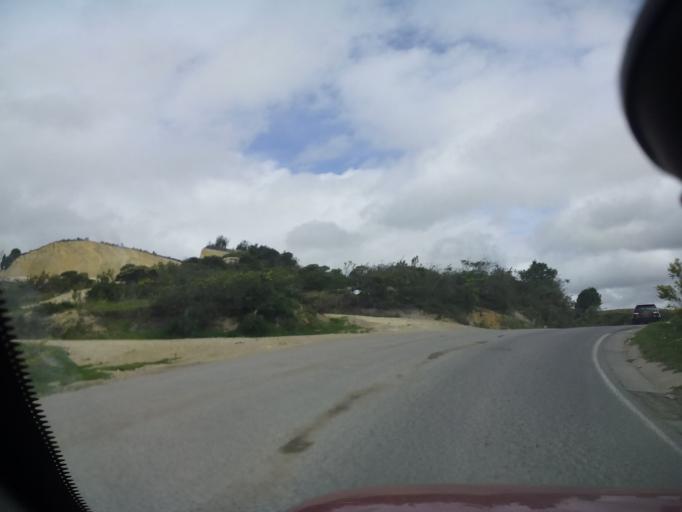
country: CO
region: Boyaca
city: Combita
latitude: 5.6349
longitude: -73.3433
